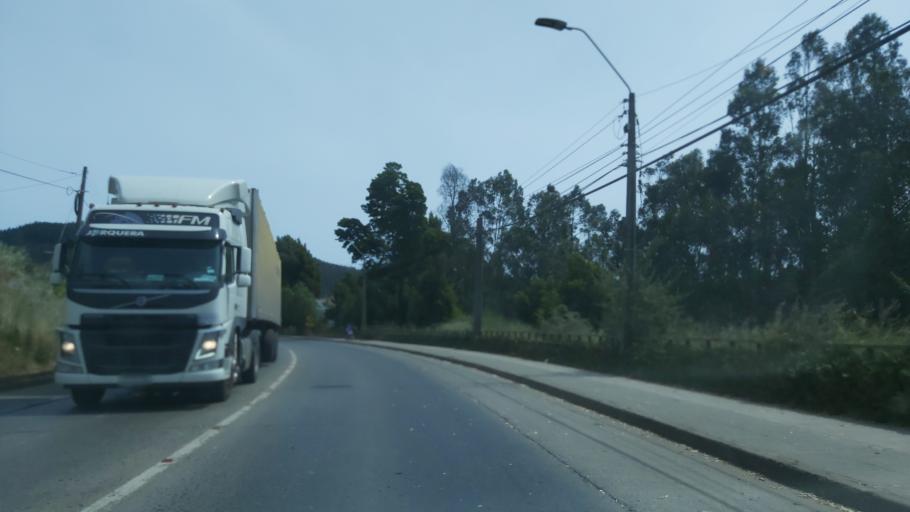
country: CL
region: Maule
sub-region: Provincia de Talca
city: Constitucion
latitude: -35.3382
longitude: -72.4200
